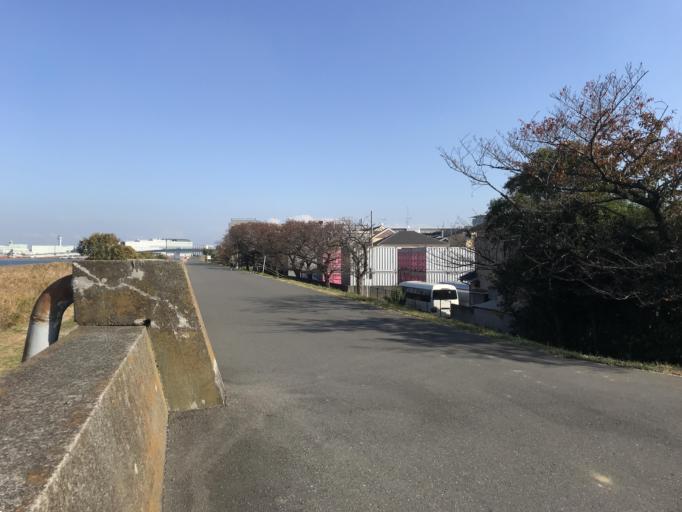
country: JP
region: Kanagawa
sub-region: Kawasaki-shi
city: Kawasaki
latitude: 35.5408
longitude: 139.7493
